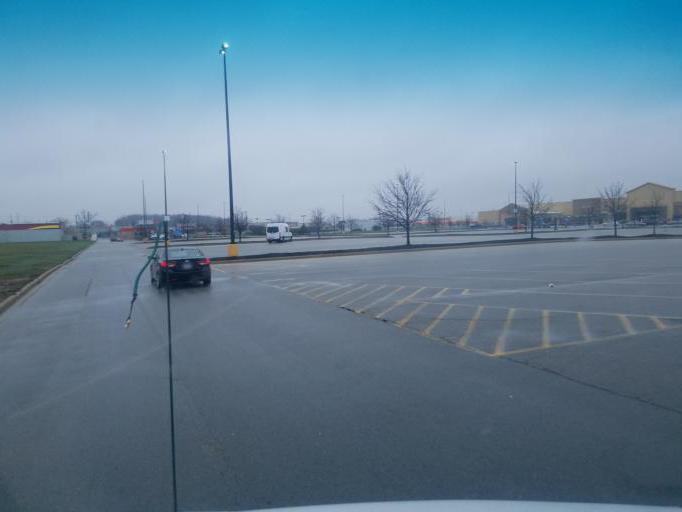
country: US
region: Ohio
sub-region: Wood County
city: Bowling Green
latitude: 41.3560
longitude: -83.6534
